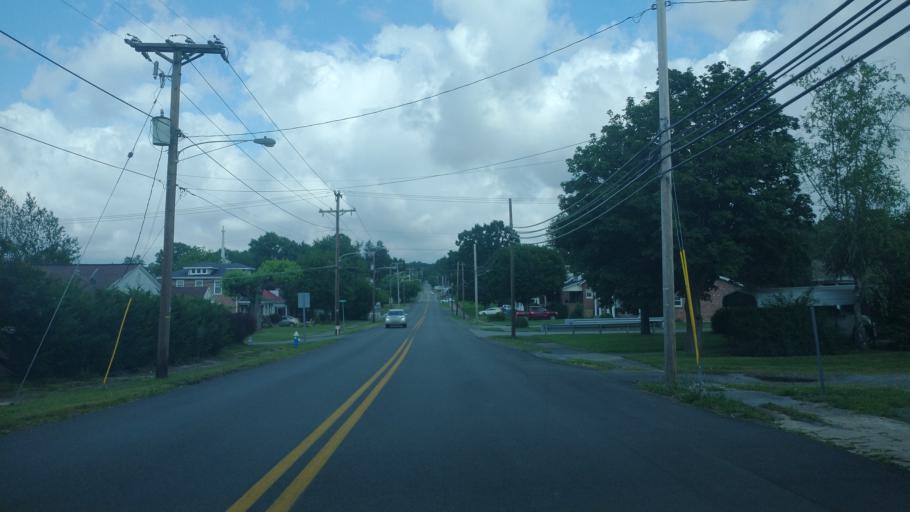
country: US
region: West Virginia
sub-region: Mercer County
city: Princeton
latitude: 37.3665
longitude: -81.1047
